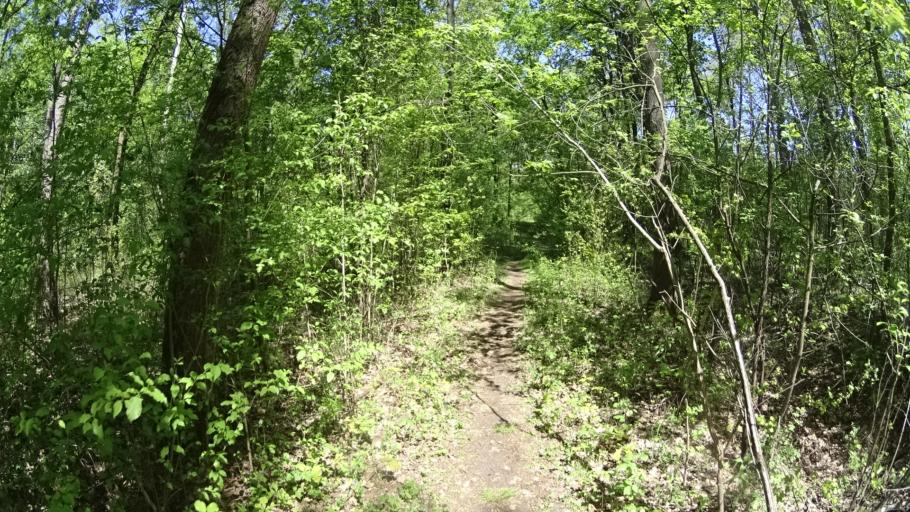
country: PL
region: Masovian Voivodeship
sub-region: Warszawa
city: Bemowo
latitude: 52.2706
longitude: 20.8840
